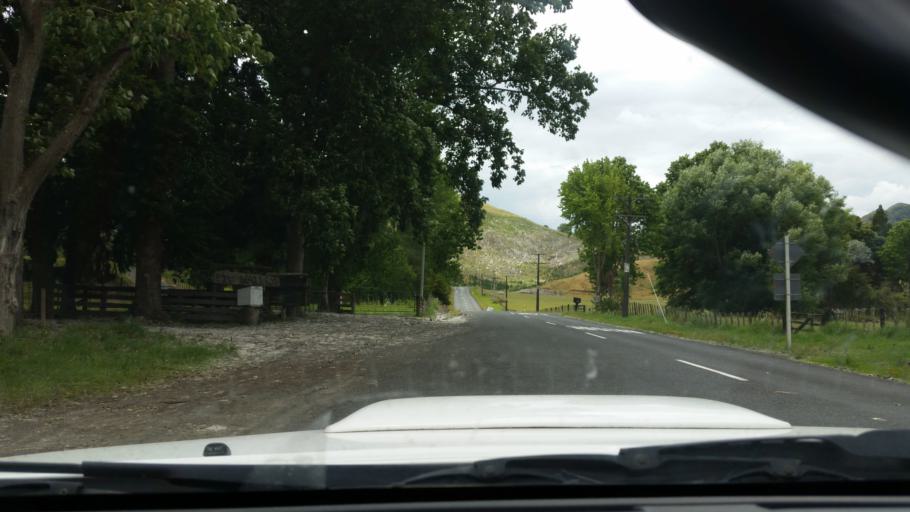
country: NZ
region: Northland
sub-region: Kaipara District
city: Dargaville
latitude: -35.7454
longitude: 173.8773
